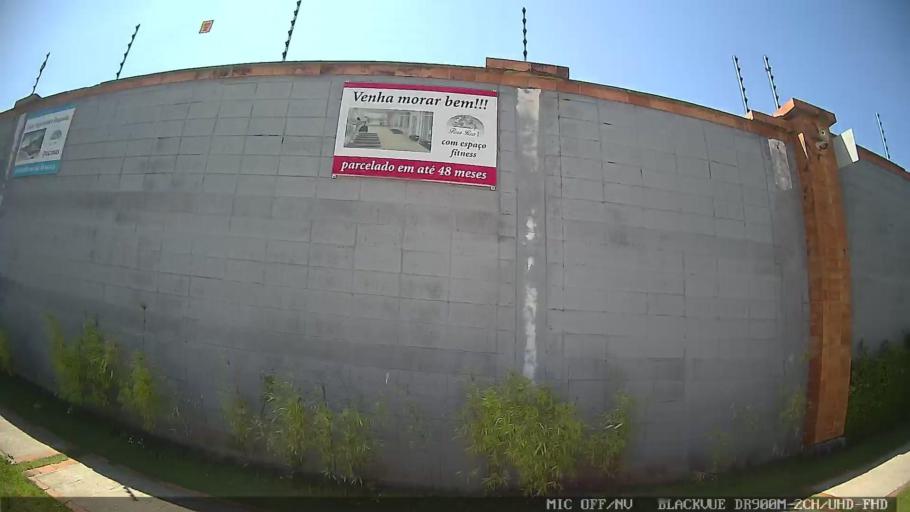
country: BR
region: Sao Paulo
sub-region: Peruibe
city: Peruibe
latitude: -24.3050
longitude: -46.9940
